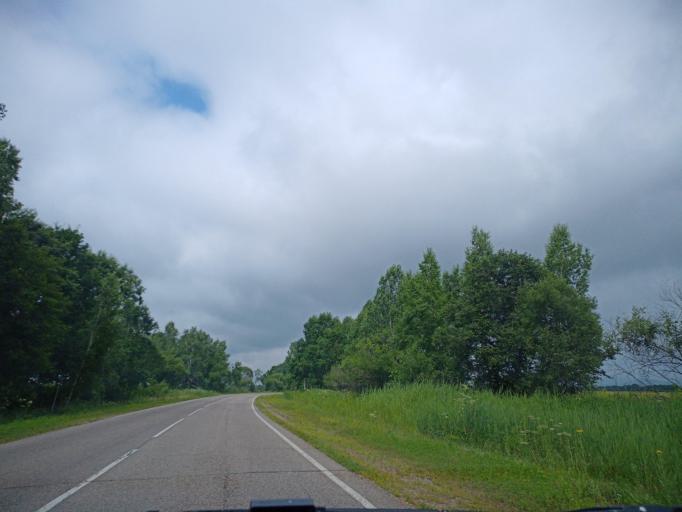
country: RU
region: Primorskiy
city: Novopokrovka
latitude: 45.9733
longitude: 134.2003
